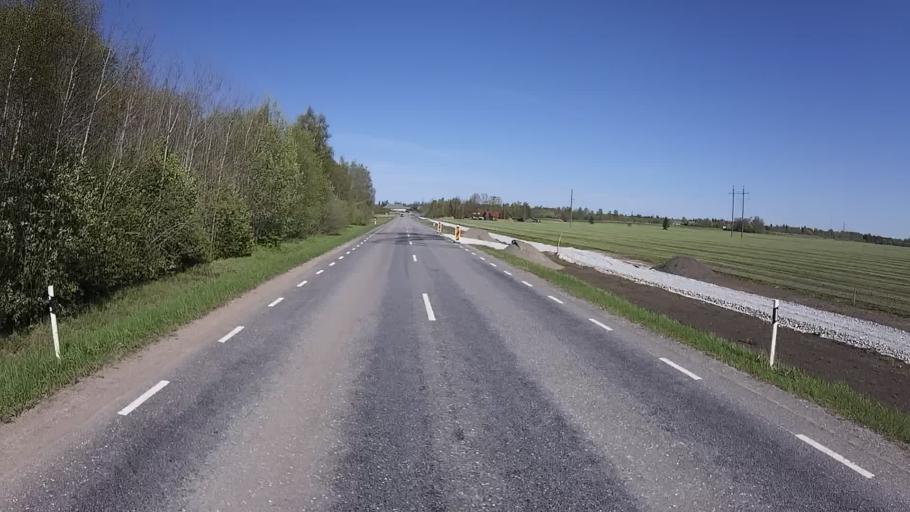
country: EE
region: Paernumaa
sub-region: Tootsi vald
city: Tootsi
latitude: 58.4989
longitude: 24.8015
